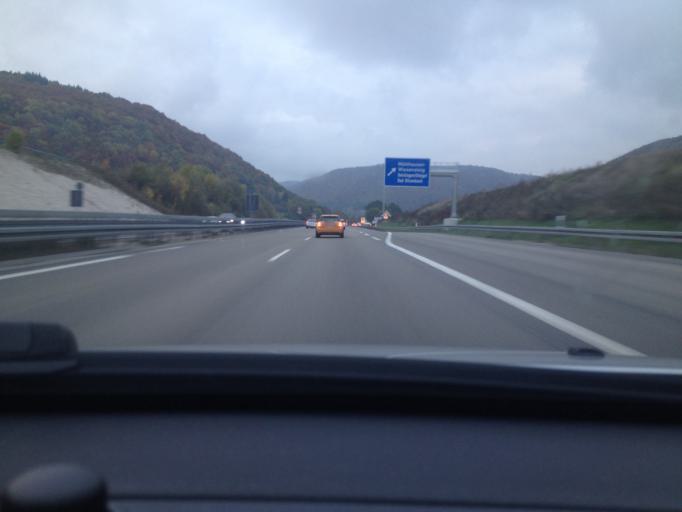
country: DE
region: Baden-Wuerttemberg
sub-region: Regierungsbezirk Stuttgart
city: Muhlhausen
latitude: 48.5852
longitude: 9.6582
